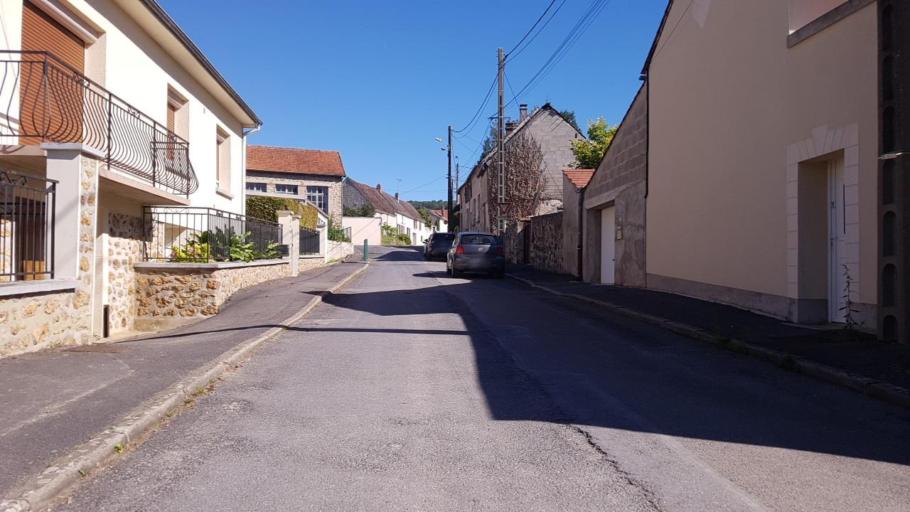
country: FR
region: Picardie
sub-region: Departement de l'Aisne
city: Chezy-sur-Marne
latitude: 49.0005
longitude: 3.3668
